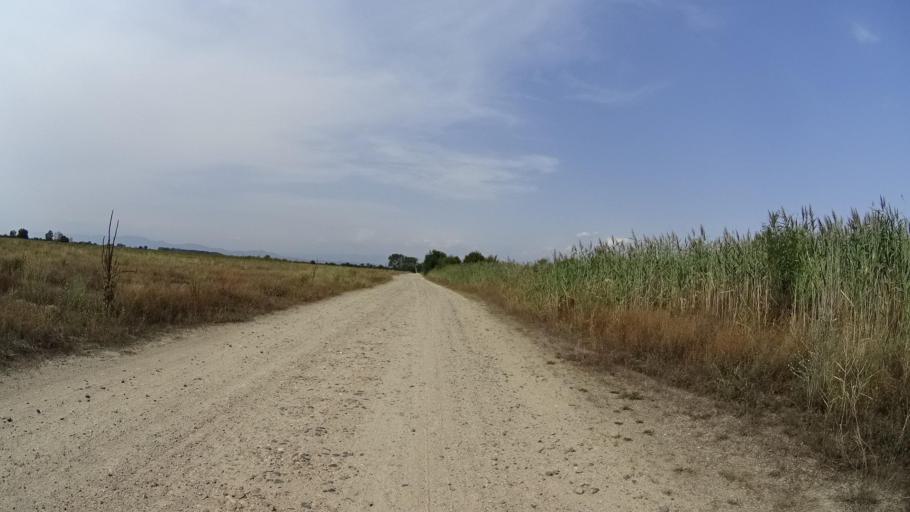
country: BG
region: Plovdiv
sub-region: Obshtina Kaloyanovo
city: Kaloyanovo
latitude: 42.2998
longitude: 24.7989
